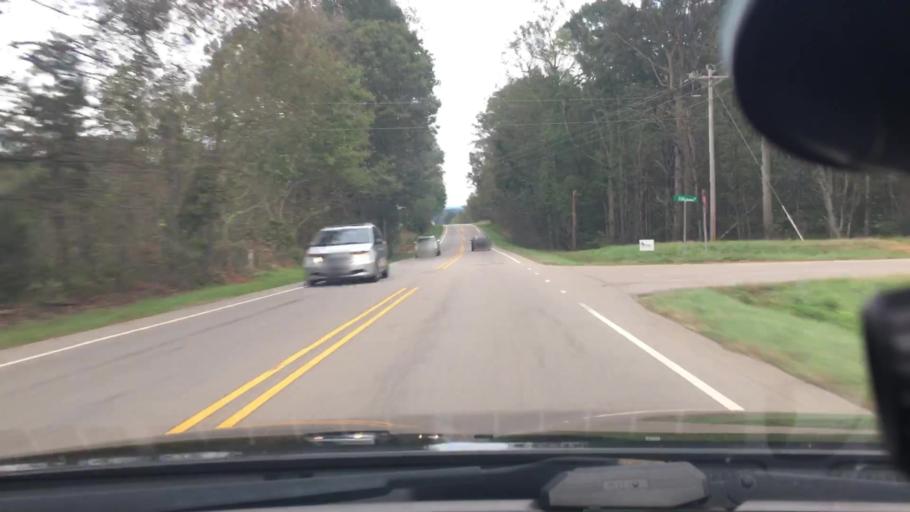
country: US
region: North Carolina
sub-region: Moore County
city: Robbins
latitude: 35.3925
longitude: -79.5209
